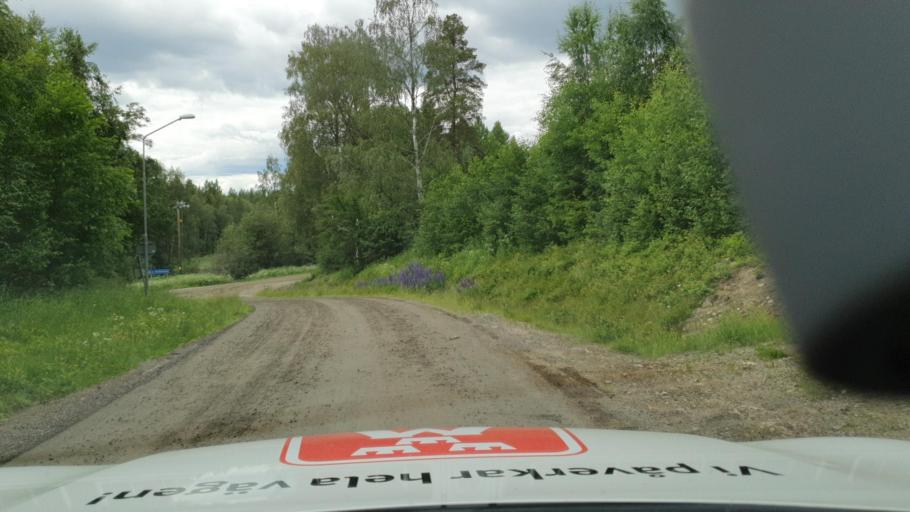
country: SE
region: Vaesterbotten
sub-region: Bjurholms Kommun
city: Bjurholm
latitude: 63.8139
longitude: 19.0353
